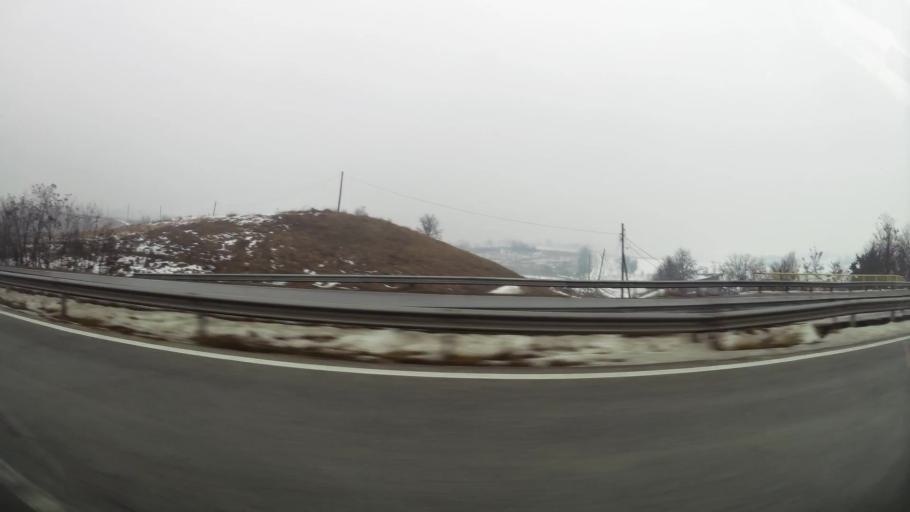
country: MK
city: Miladinovci
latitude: 41.9738
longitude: 21.6488
